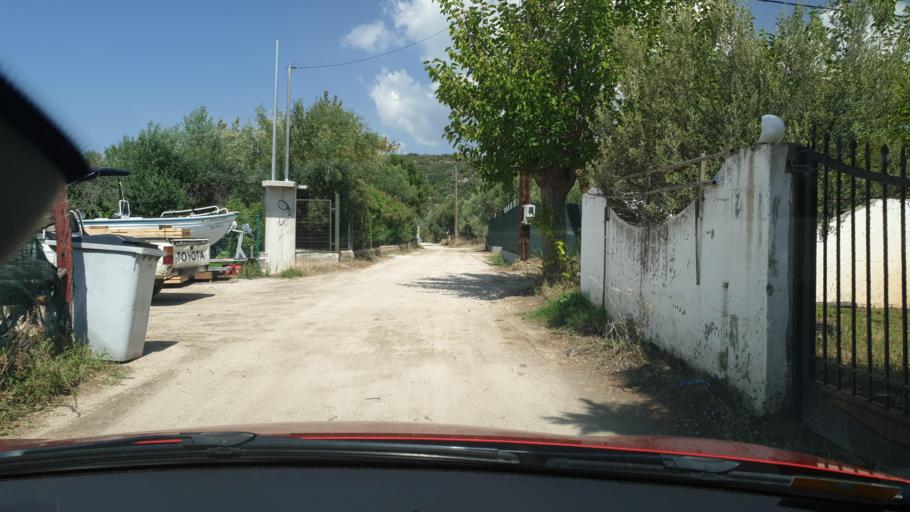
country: GR
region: Central Macedonia
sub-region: Nomos Chalkidikis
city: Sykia
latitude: 39.9841
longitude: 23.9087
